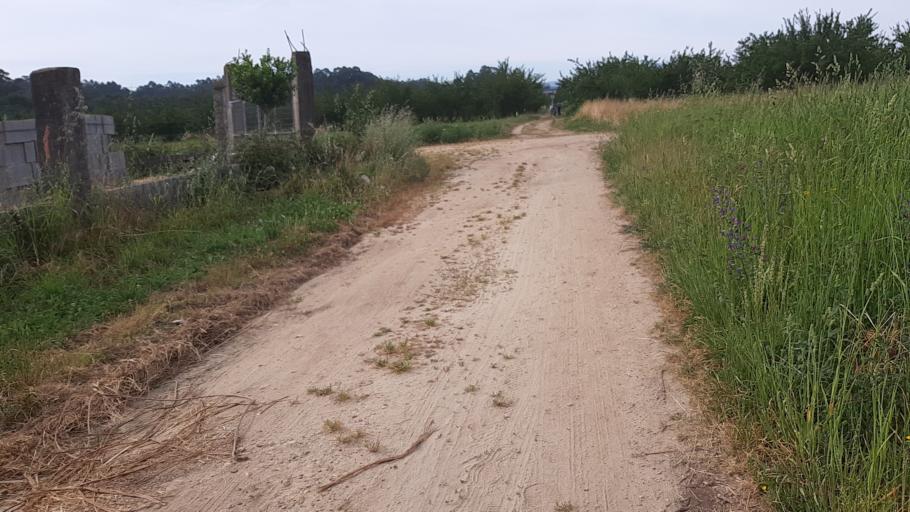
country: ES
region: Galicia
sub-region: Provincia de Pontevedra
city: O Rosal
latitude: 41.9266
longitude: -8.8293
